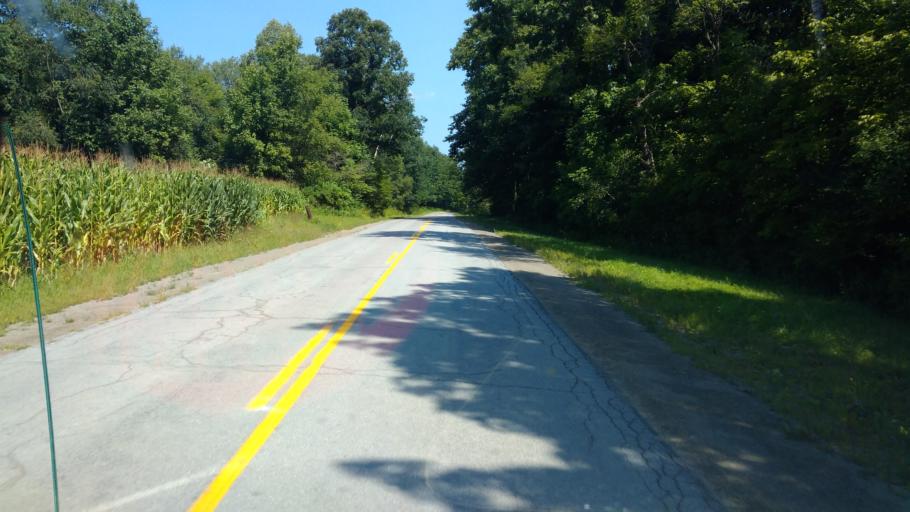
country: US
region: New York
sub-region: Allegany County
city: Belmont
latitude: 42.2825
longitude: -78.0554
